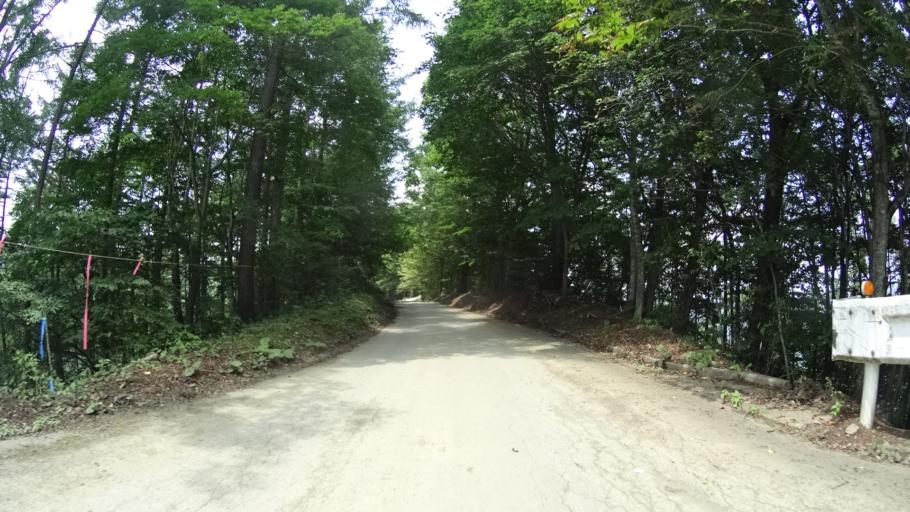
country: JP
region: Nagano
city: Saku
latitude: 36.0976
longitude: 138.6738
